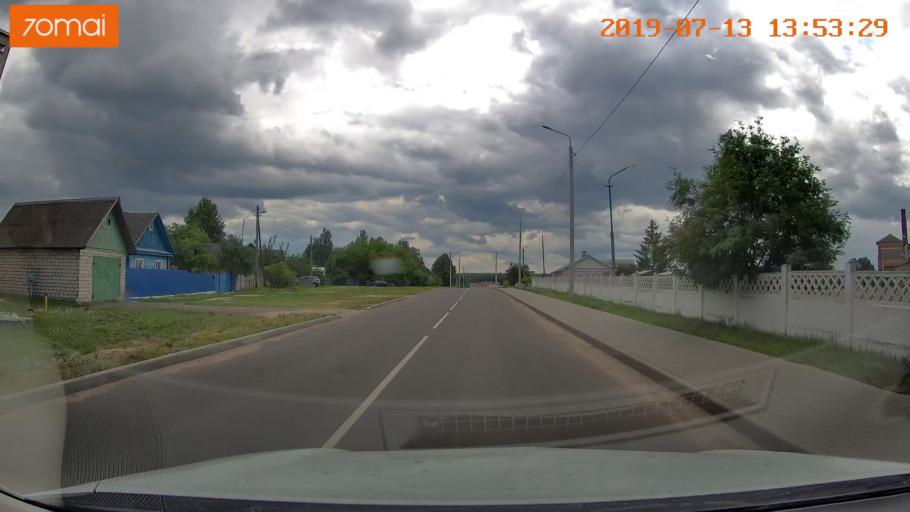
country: BY
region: Mogilev
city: Asipovichy
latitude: 53.2925
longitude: 28.6485
